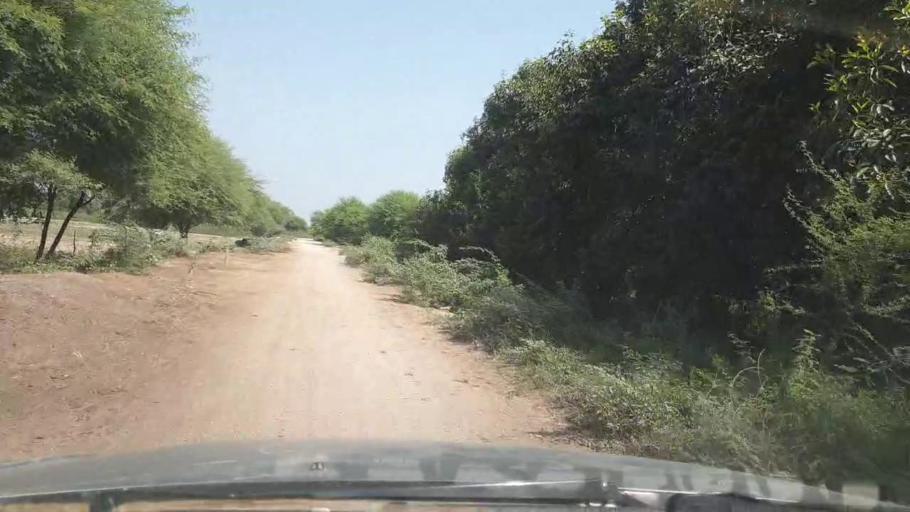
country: PK
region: Sindh
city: Tando Ghulam Ali
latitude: 25.1589
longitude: 68.8885
